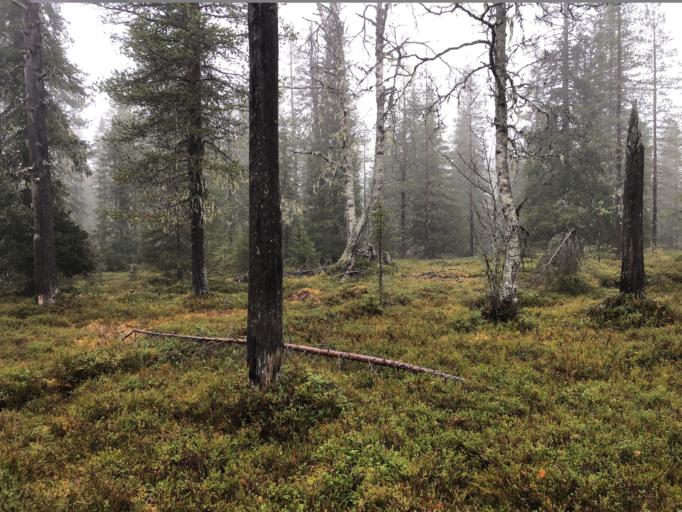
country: FI
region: Lapland
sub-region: Itae-Lappi
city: Posio
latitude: 66.3206
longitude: 28.4420
